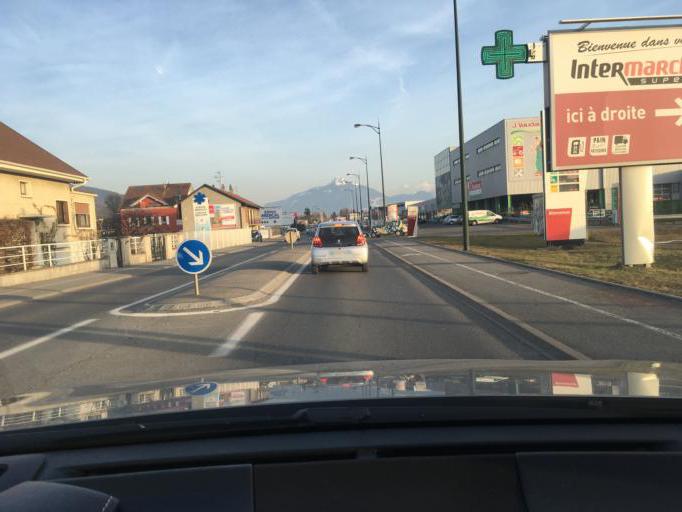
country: FR
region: Rhone-Alpes
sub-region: Departement de la Haute-Savoie
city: Cranves-Sales
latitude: 46.1852
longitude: 6.2768
